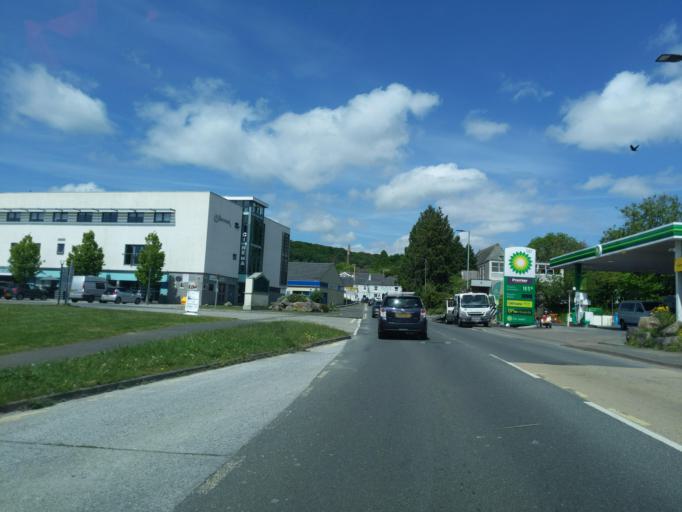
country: GB
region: England
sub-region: Devon
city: Ivybridge
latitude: 50.3891
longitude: -3.9186
